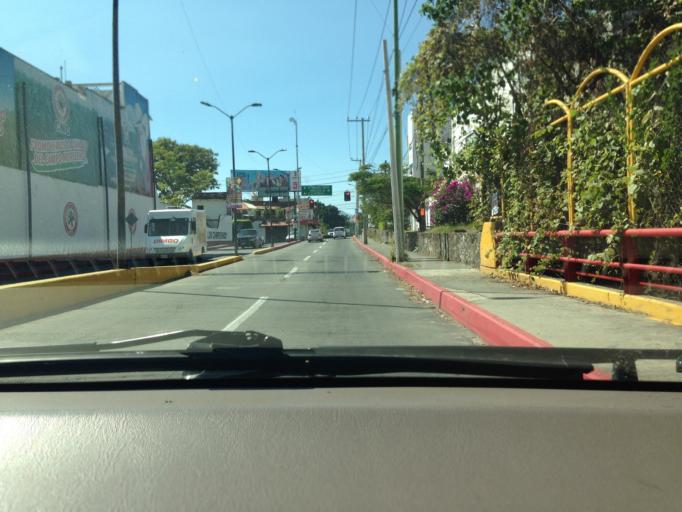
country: MX
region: Morelos
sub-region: Cuernavaca
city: Fraccionamiento Lomas de Ahuatlan
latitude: 18.9556
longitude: -99.2411
